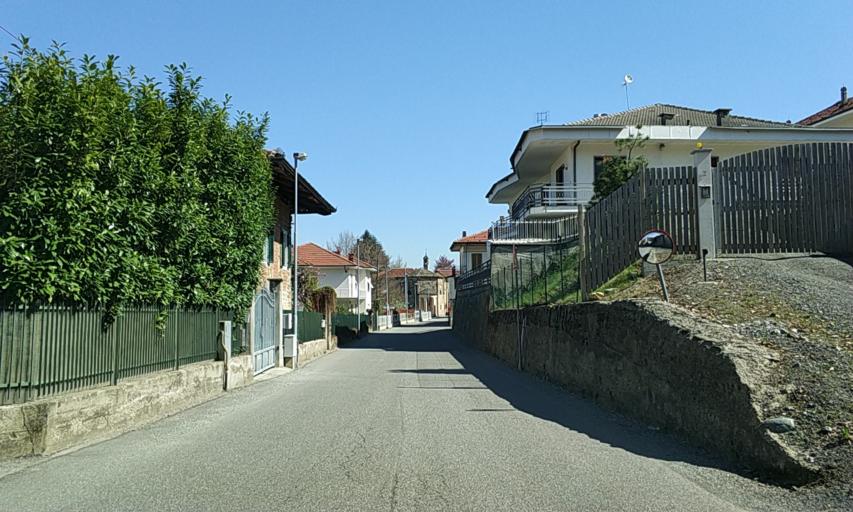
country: IT
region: Piedmont
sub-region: Provincia di Torino
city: Forno Canavese
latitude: 45.3410
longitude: 7.5856
